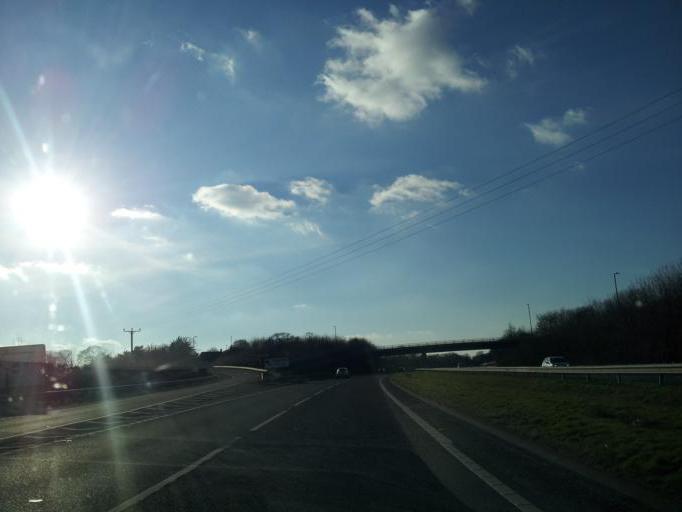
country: GB
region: England
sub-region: Devon
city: Crediton
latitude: 50.7267
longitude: -3.7241
